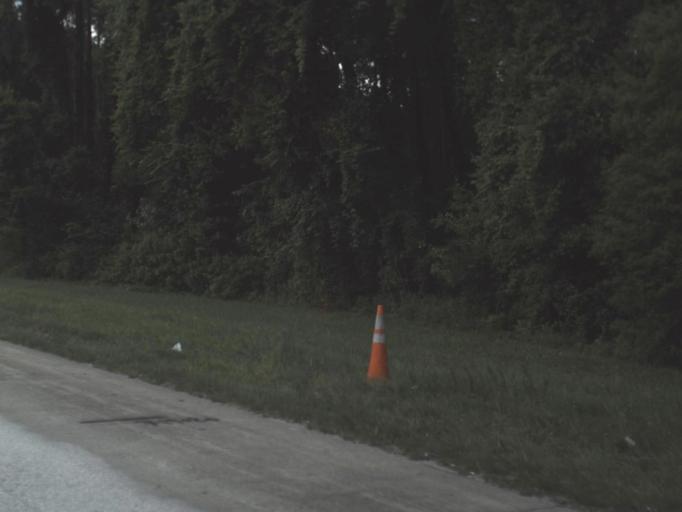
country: US
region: Florida
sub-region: Duval County
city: Jacksonville
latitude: 30.2301
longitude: -81.5771
